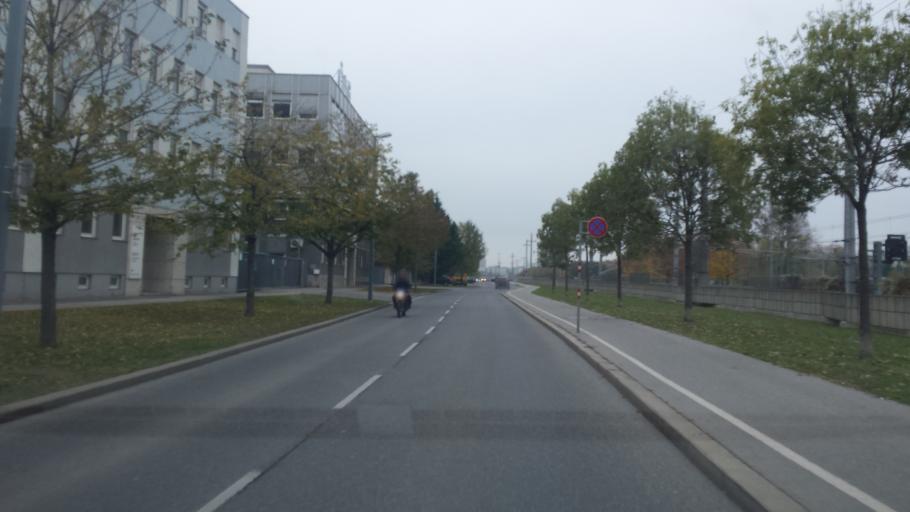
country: AT
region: Lower Austria
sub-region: Politischer Bezirk Wien-Umgebung
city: Schwechat
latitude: 48.1608
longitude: 16.4211
